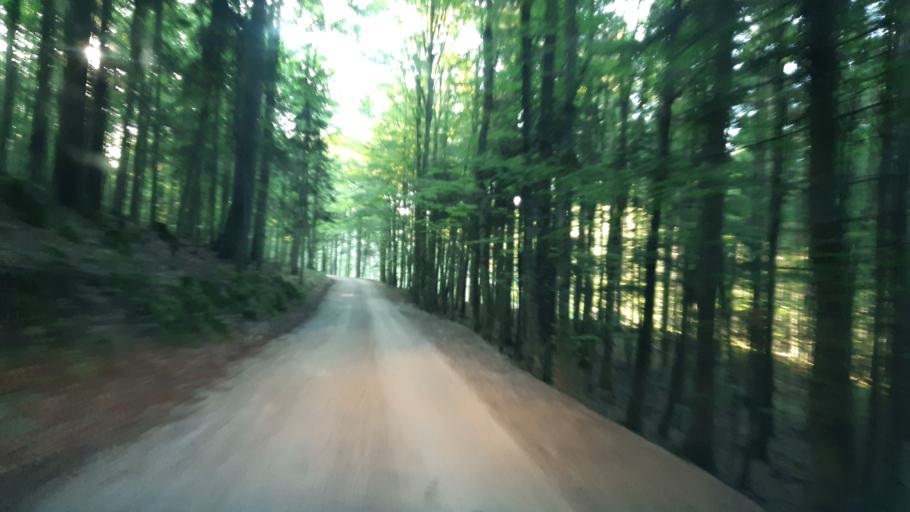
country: SI
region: Dolenjske Toplice
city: Dolenjske Toplice
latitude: 45.6752
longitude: 14.9780
